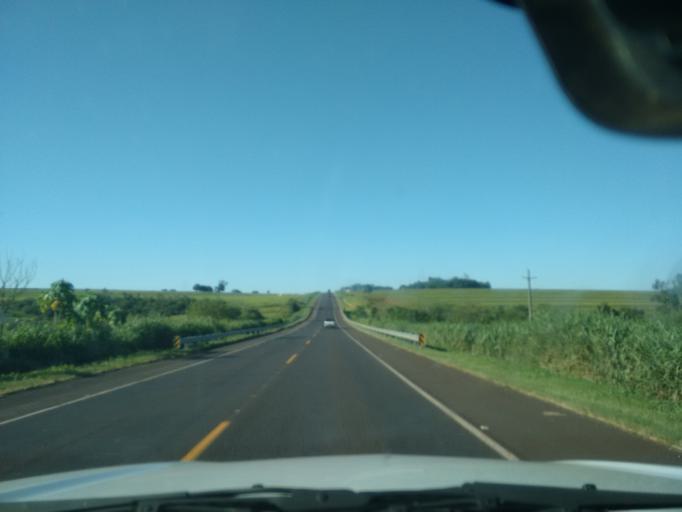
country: PY
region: Canindeyu
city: Salto del Guaira
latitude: -23.9819
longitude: -54.3311
